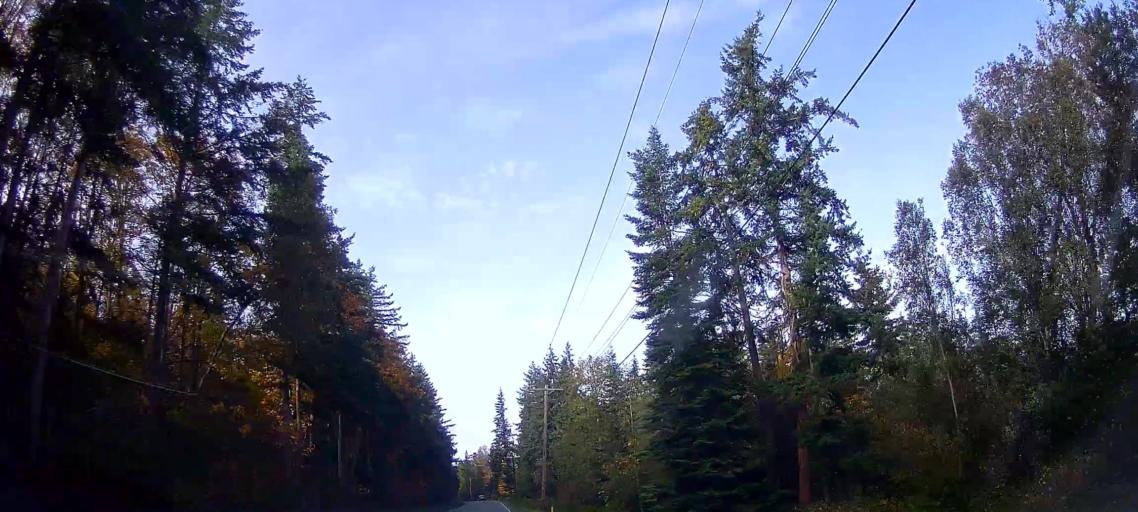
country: US
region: Washington
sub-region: Snohomish County
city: Stanwood
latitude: 48.2450
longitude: -122.4600
